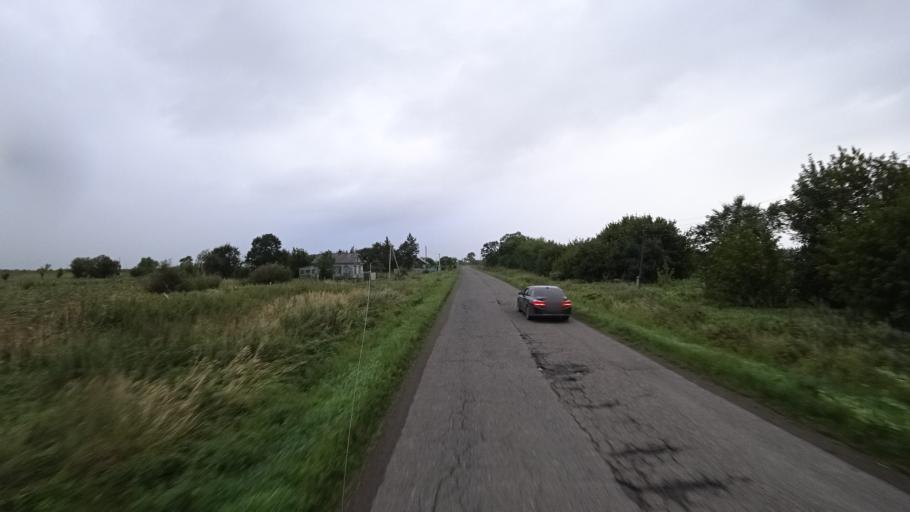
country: RU
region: Primorskiy
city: Chernigovka
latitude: 44.3965
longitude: 132.5279
